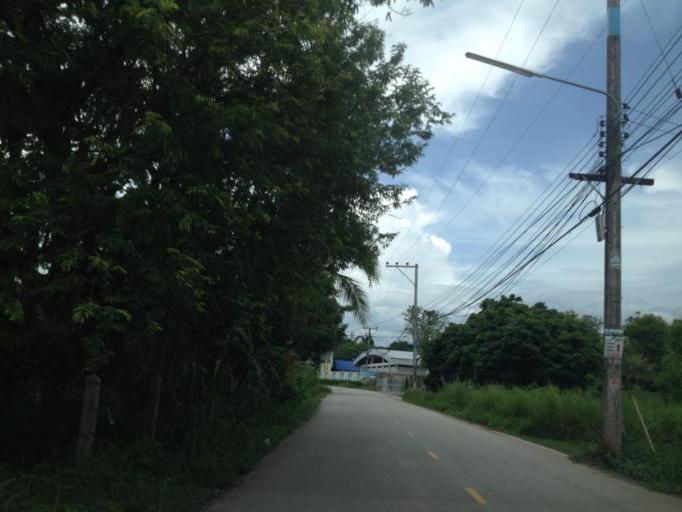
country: TH
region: Chiang Mai
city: Hang Dong
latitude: 18.6865
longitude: 98.8895
